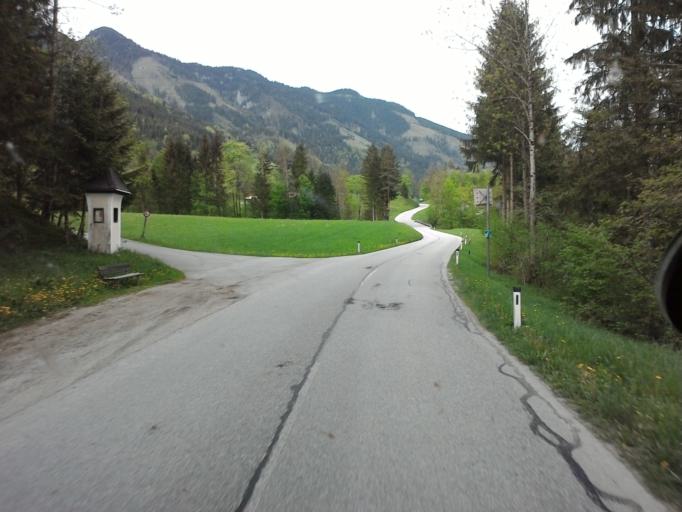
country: AT
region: Styria
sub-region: Politischer Bezirk Liezen
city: Palfau
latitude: 47.6998
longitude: 14.7898
